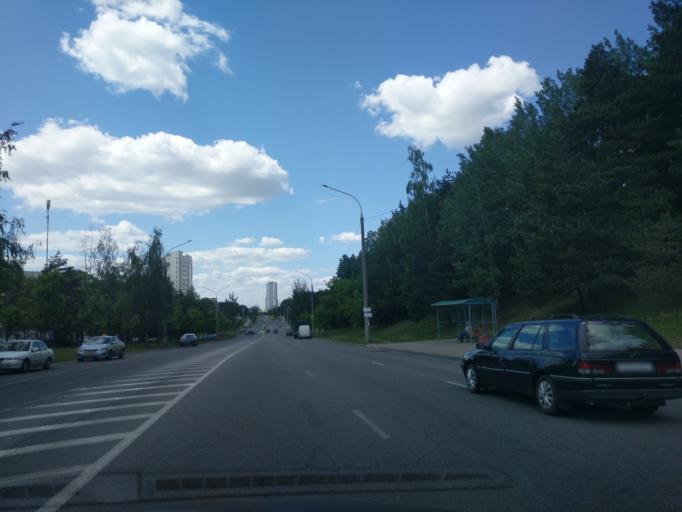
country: BY
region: Minsk
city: Borovlyany
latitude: 53.9238
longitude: 27.6714
